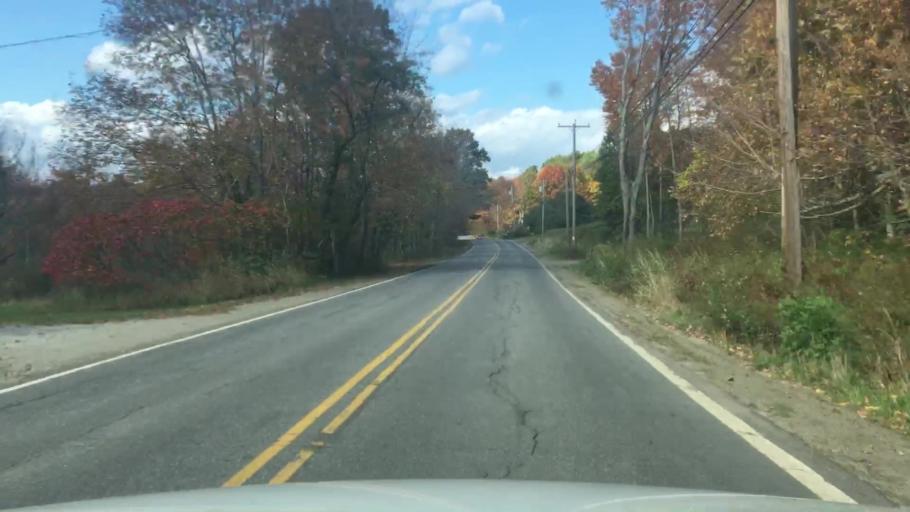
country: US
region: Maine
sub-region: Knox County
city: Union
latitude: 44.2059
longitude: -69.2618
